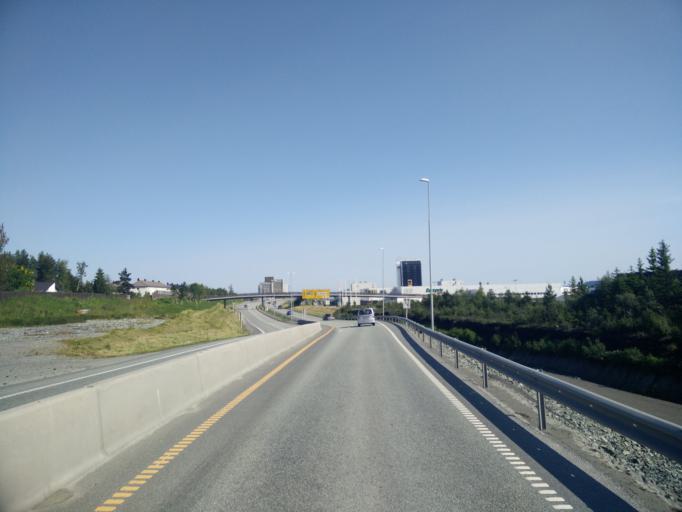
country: NO
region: Sor-Trondelag
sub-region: Trondheim
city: Trondheim
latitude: 63.3539
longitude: 10.3704
